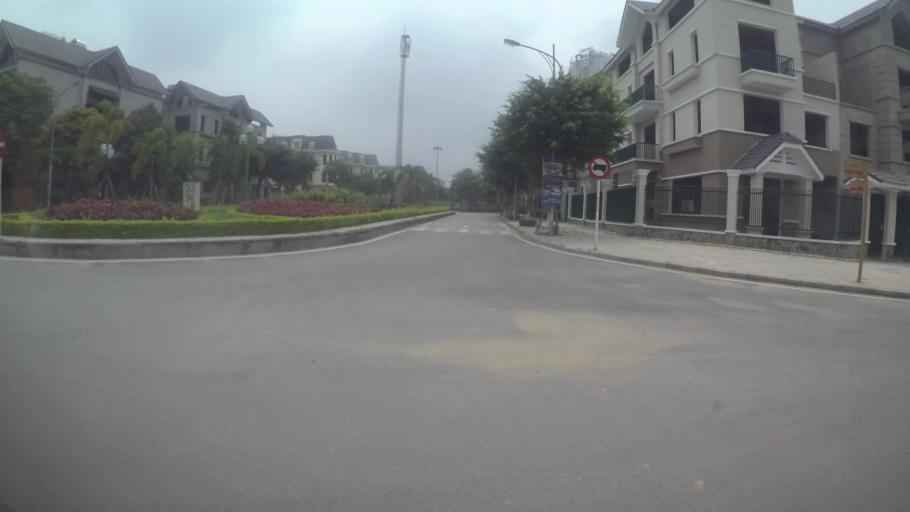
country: VN
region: Ha Noi
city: Ha Dong
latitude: 20.9793
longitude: 105.7595
